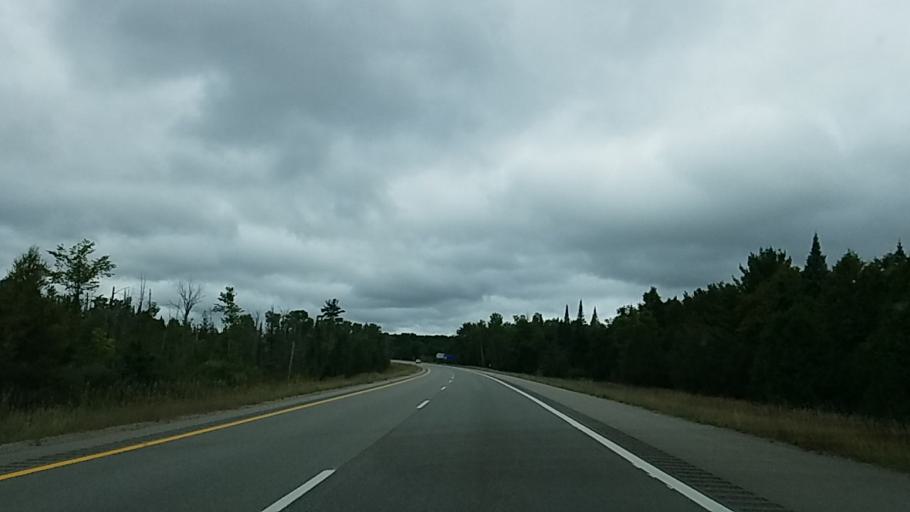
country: US
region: Michigan
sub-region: Otsego County
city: Gaylord
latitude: 45.1615
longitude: -84.6624
